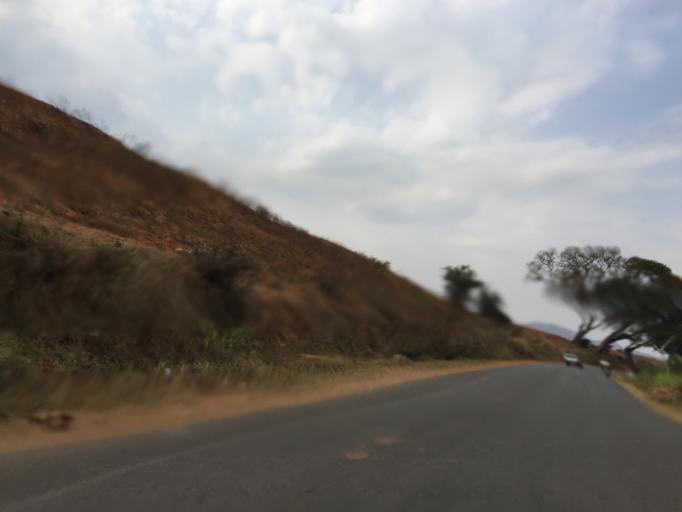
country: IN
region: Karnataka
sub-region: Chikkaballapur
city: Chik Ballapur
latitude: 13.4183
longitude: 77.7201
